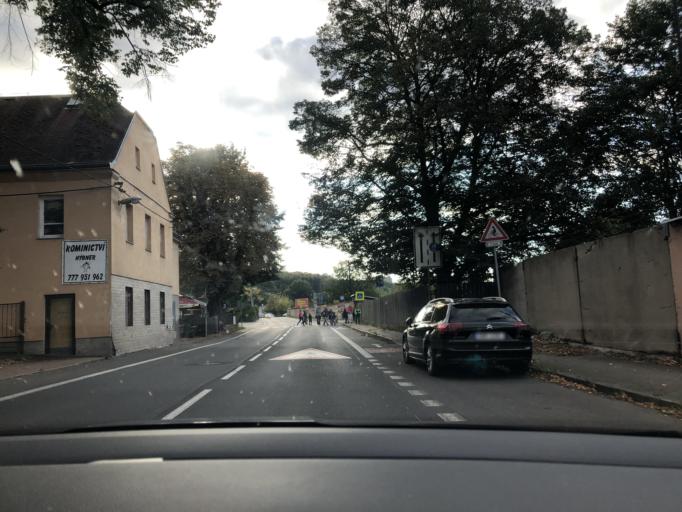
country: CZ
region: Ustecky
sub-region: Okres Usti nad Labem
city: Usti nad Labem
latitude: 50.6599
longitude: 14.0826
